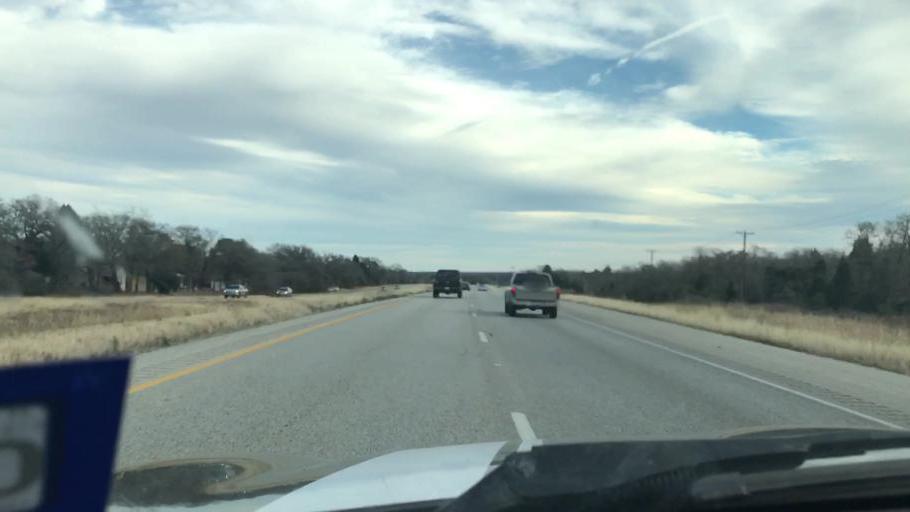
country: US
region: Texas
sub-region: Bastrop County
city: Elgin
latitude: 30.3249
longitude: -97.3276
